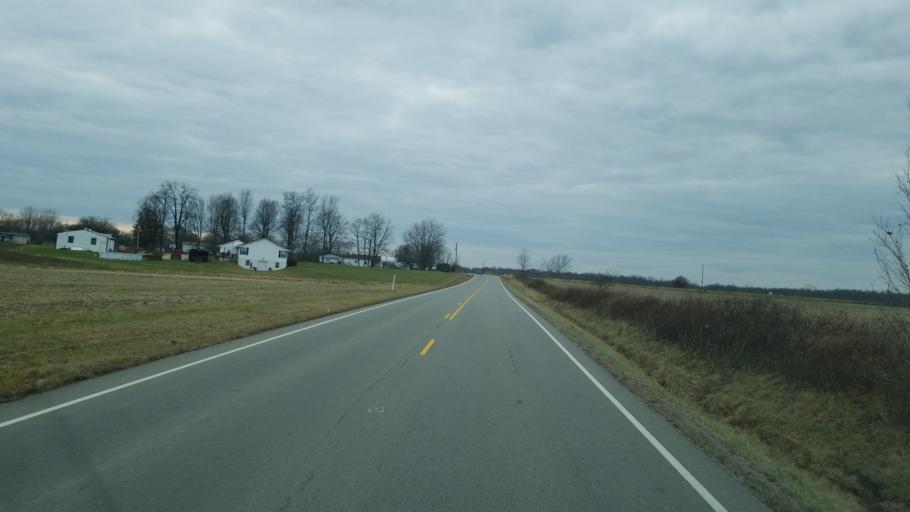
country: US
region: Ohio
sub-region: Highland County
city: Hillsboro
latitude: 39.2163
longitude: -83.4613
